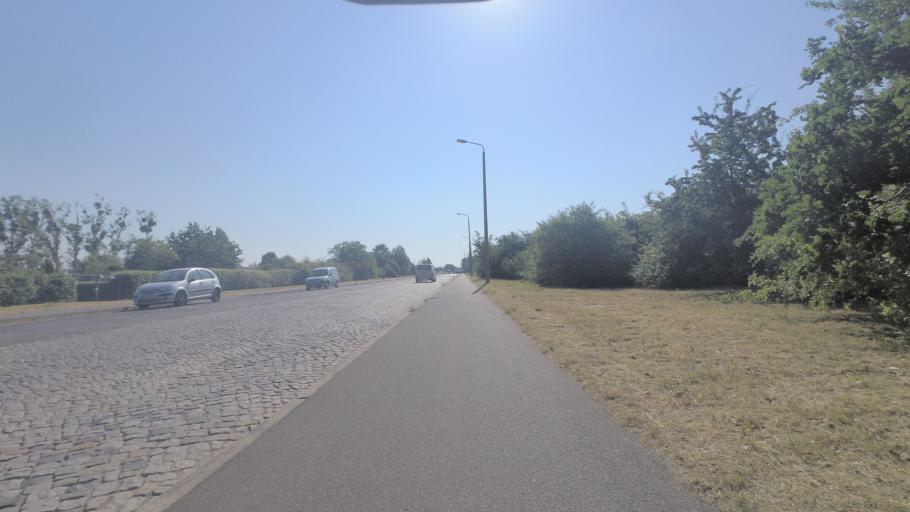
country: DE
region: Saxony-Anhalt
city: Dessau
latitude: 51.8375
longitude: 12.1968
